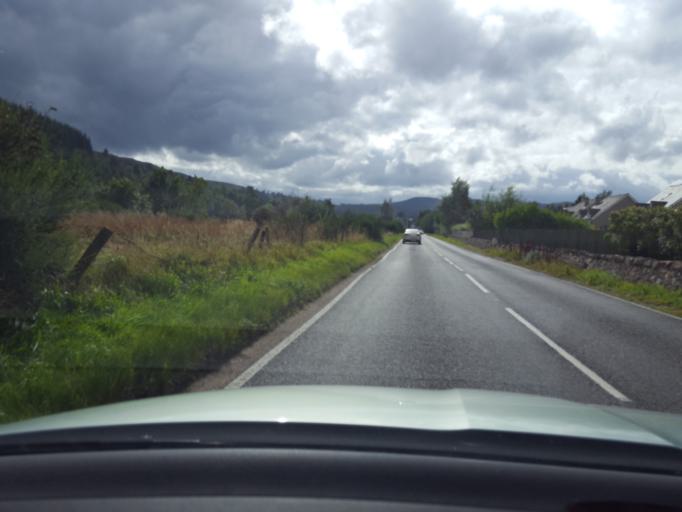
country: GB
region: Scotland
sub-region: Aberdeenshire
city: Ballater
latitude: 57.0527
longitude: -3.0301
